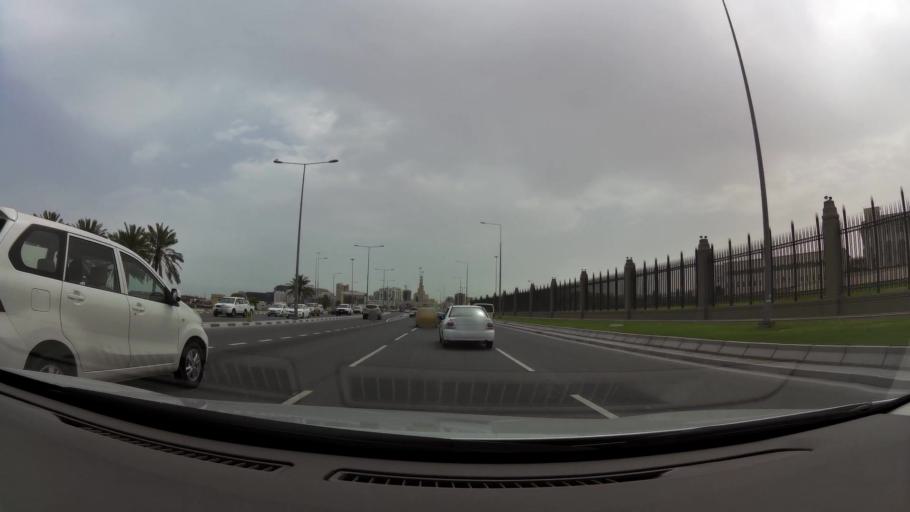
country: QA
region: Baladiyat ad Dawhah
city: Doha
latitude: 25.2930
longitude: 51.5278
